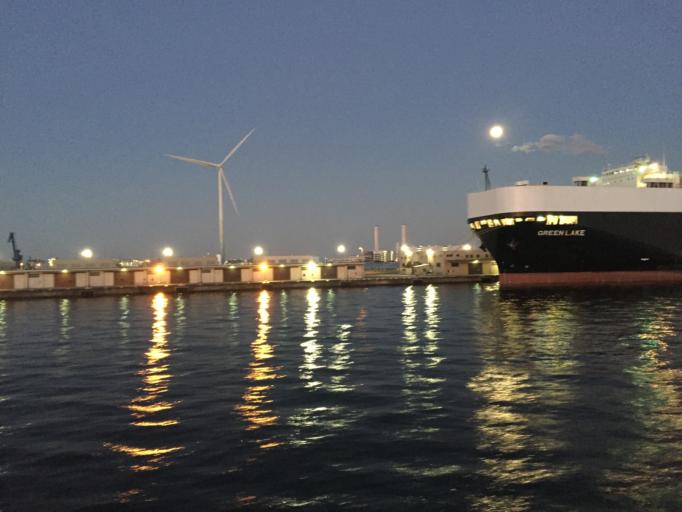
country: JP
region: Kanagawa
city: Yokohama
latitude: 35.4648
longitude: 139.6486
